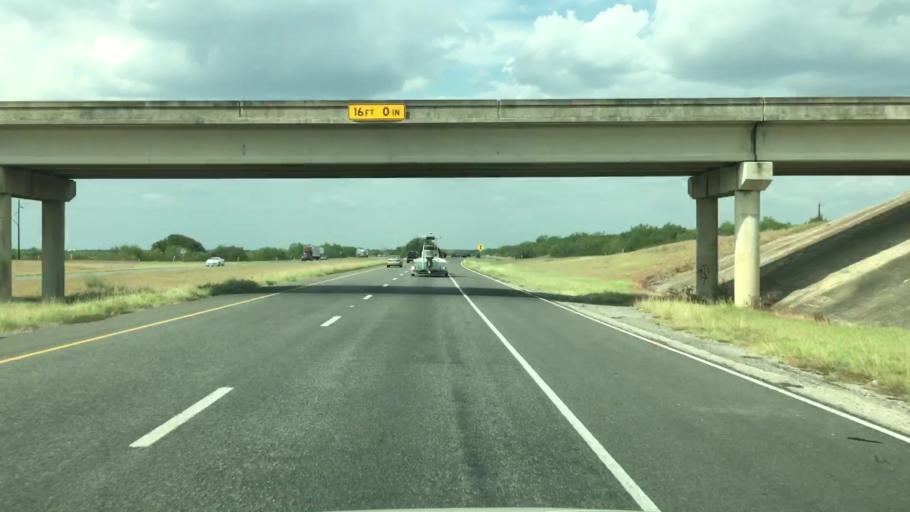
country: US
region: Texas
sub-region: Atascosa County
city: Pleasanton
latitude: 28.9161
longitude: -98.4346
